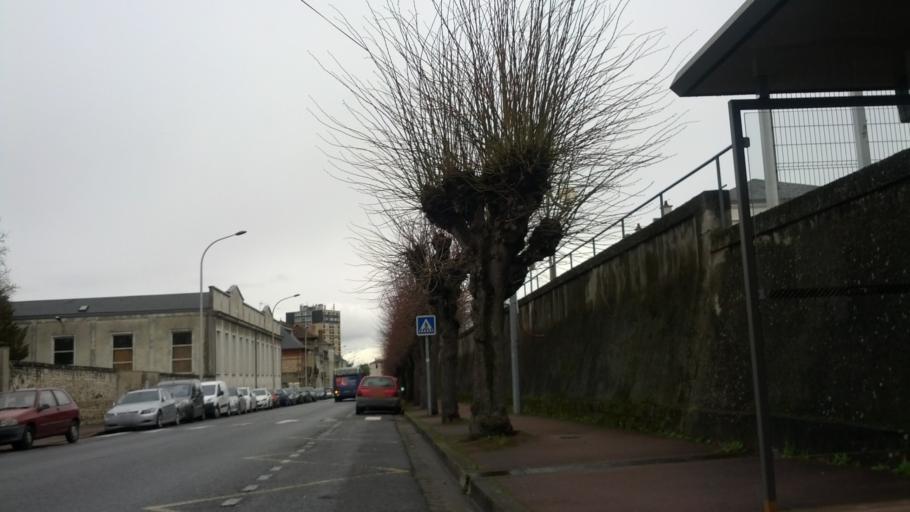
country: FR
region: Poitou-Charentes
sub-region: Departement de la Vienne
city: Chatellerault
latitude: 46.8188
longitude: 0.5488
